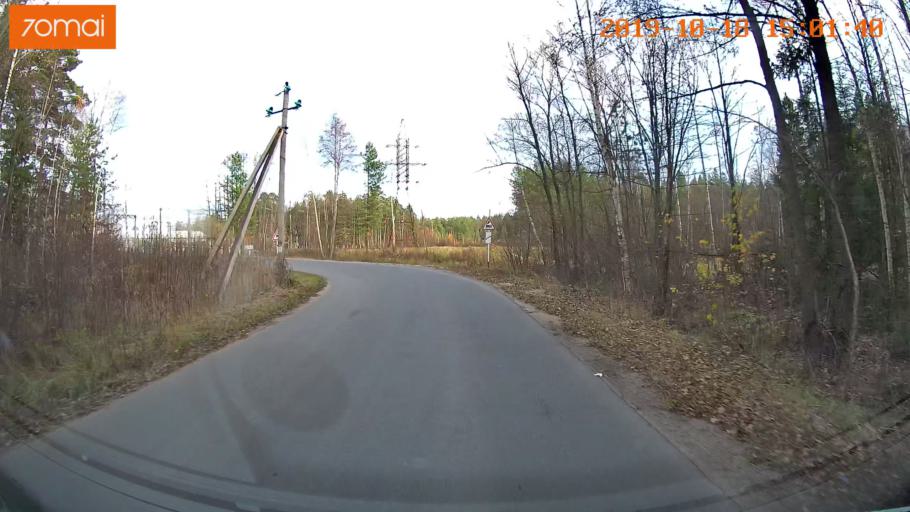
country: RU
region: Vladimir
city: Gus'-Khrustal'nyy
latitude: 55.5004
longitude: 40.6076
